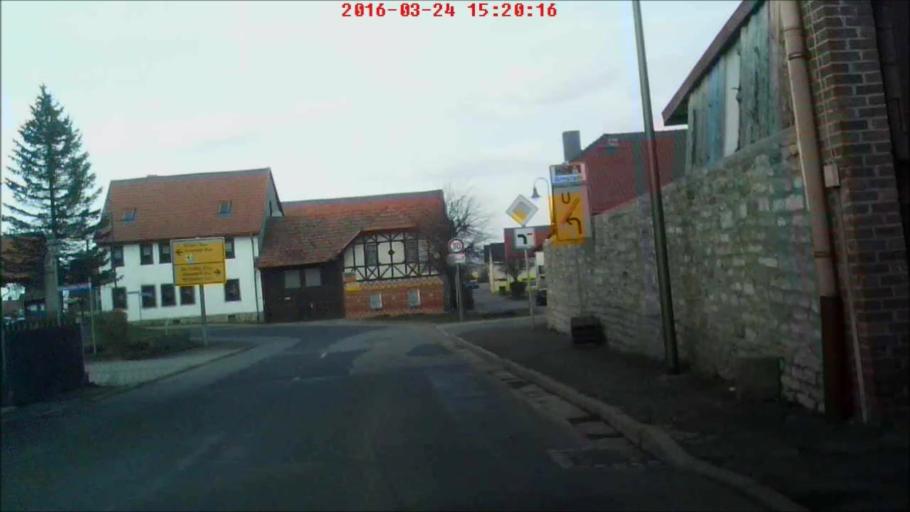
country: DE
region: Thuringia
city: Bosleben-Wullersleben
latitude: 50.8128
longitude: 11.0694
